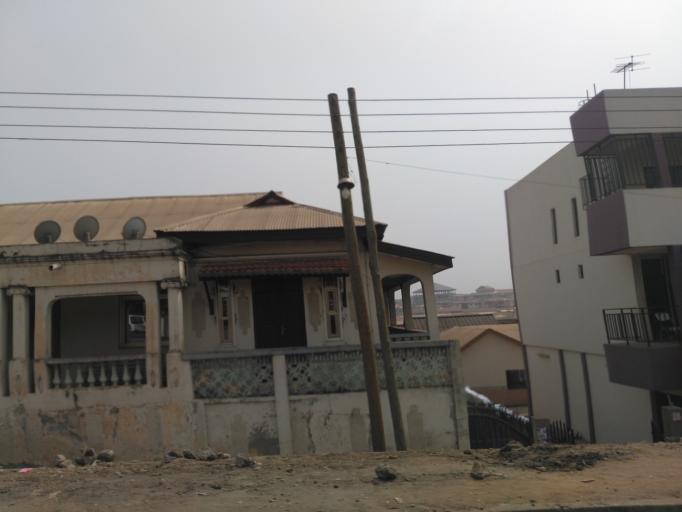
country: GH
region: Ashanti
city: Kumasi
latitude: 6.7120
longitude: -1.6217
